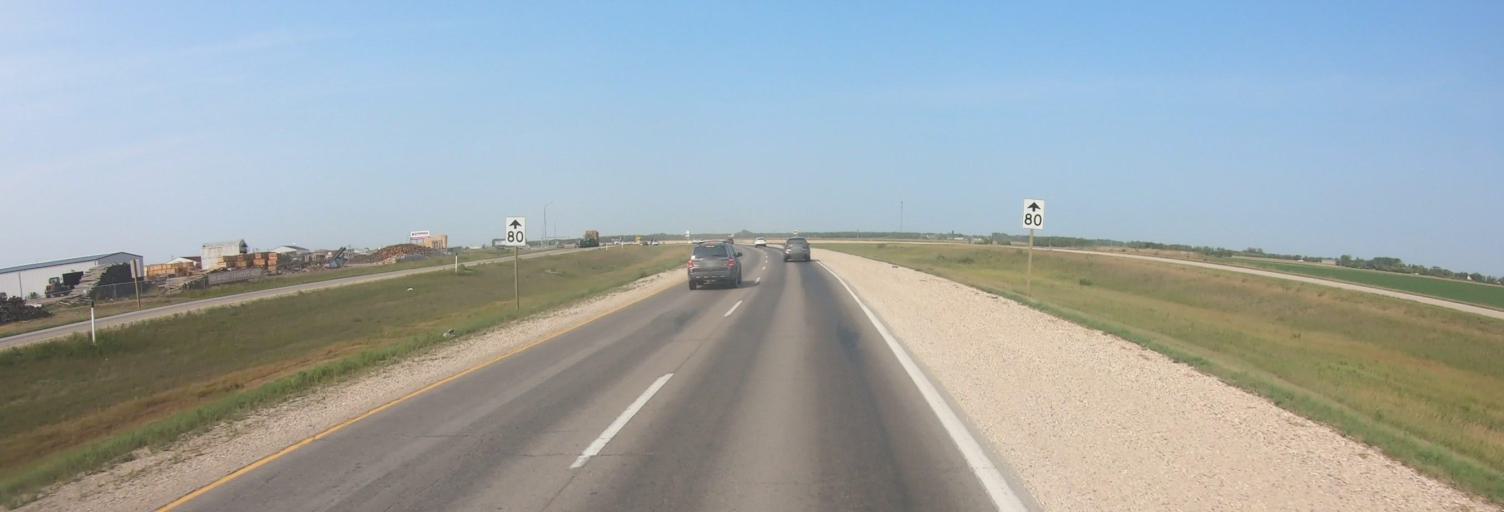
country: CA
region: Manitoba
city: Steinbach
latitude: 49.5998
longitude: -96.6842
